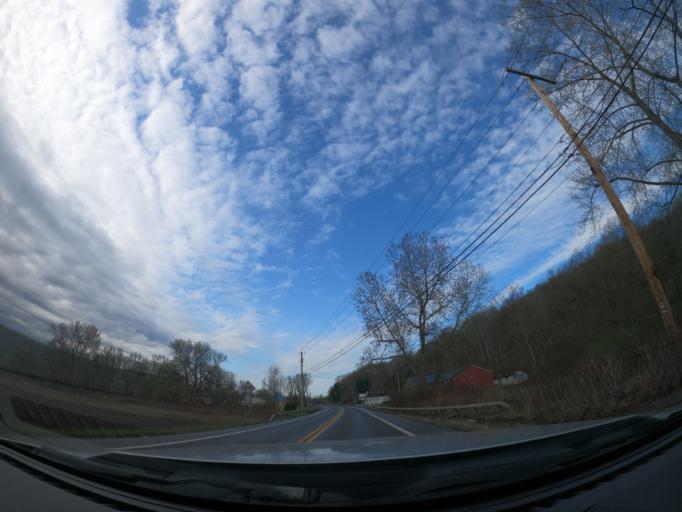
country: US
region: New York
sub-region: Cortland County
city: Homer
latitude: 42.6358
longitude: -76.1439
